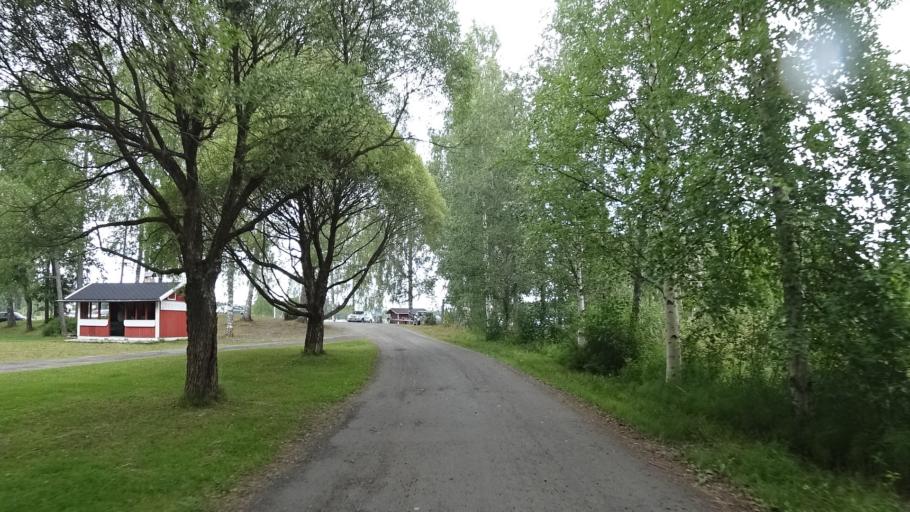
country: FI
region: North Karelia
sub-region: Keski-Karjala
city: Kesaelahti
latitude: 62.0956
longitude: 29.8753
